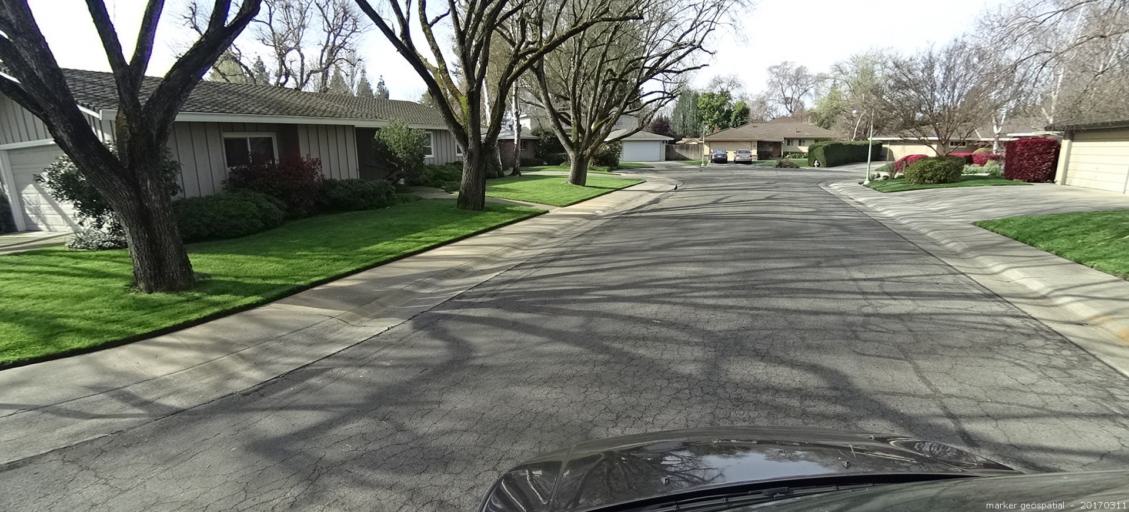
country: US
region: California
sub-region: Yolo County
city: West Sacramento
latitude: 38.5108
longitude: -121.5491
